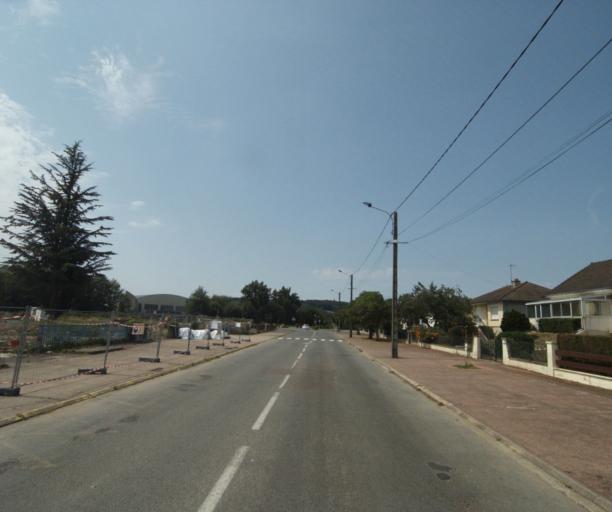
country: FR
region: Bourgogne
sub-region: Departement de Saone-et-Loire
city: Gueugnon
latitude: 46.6007
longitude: 4.0508
